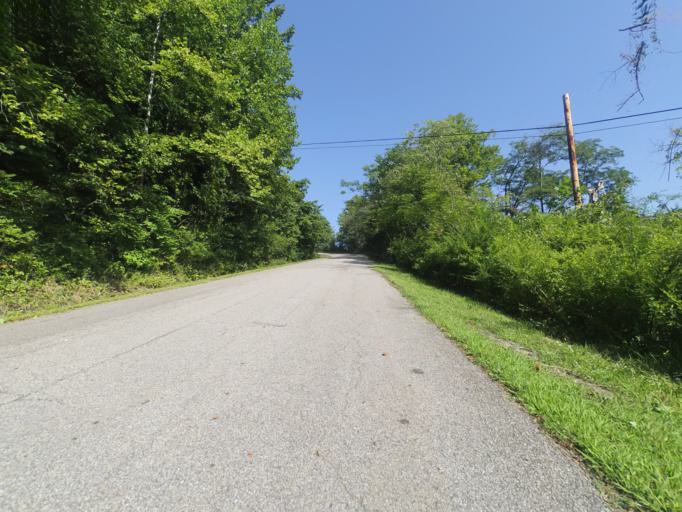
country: US
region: West Virginia
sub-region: Cabell County
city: Huntington
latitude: 38.3959
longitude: -82.4688
